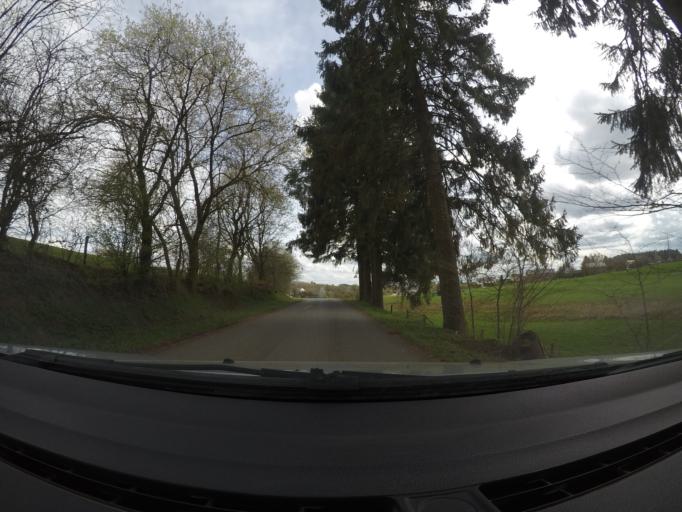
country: BE
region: Wallonia
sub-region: Province du Luxembourg
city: Neufchateau
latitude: 49.8192
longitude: 5.4680
